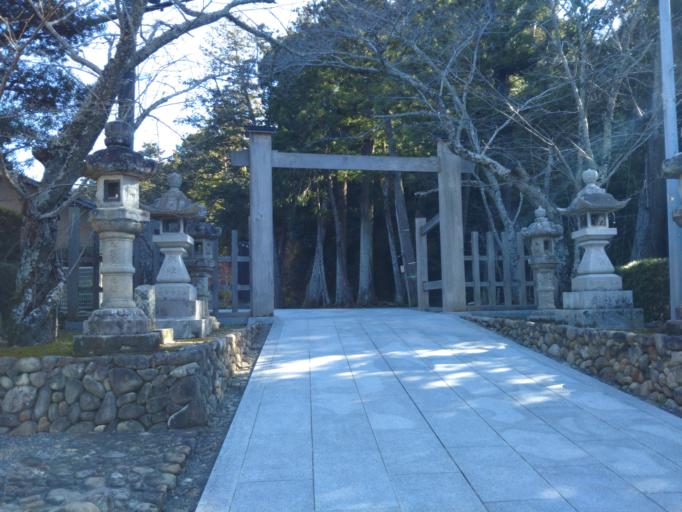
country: JP
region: Shizuoka
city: Kakegawa
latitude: 34.7345
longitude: 137.9718
